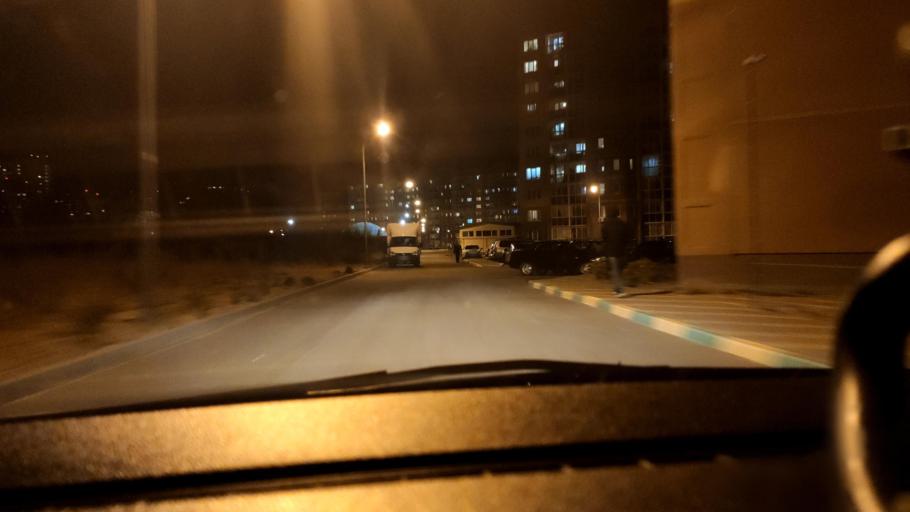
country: RU
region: Voronezj
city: Shilovo
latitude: 51.5722
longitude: 39.1294
